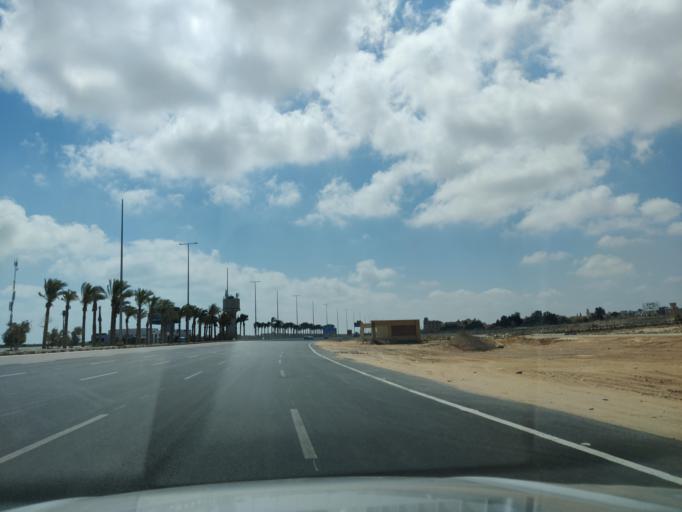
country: EG
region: Muhafazat Matruh
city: Al `Alamayn
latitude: 30.8447
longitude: 28.9421
